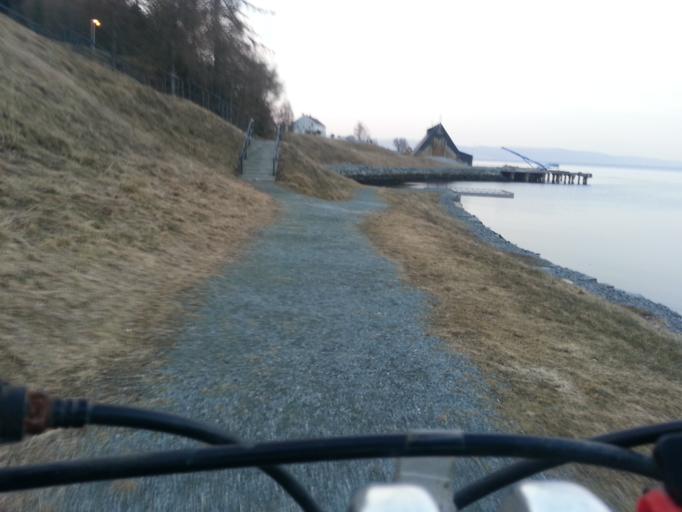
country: NO
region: Sor-Trondelag
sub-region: Trondheim
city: Trondheim
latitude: 63.4347
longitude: 10.3506
